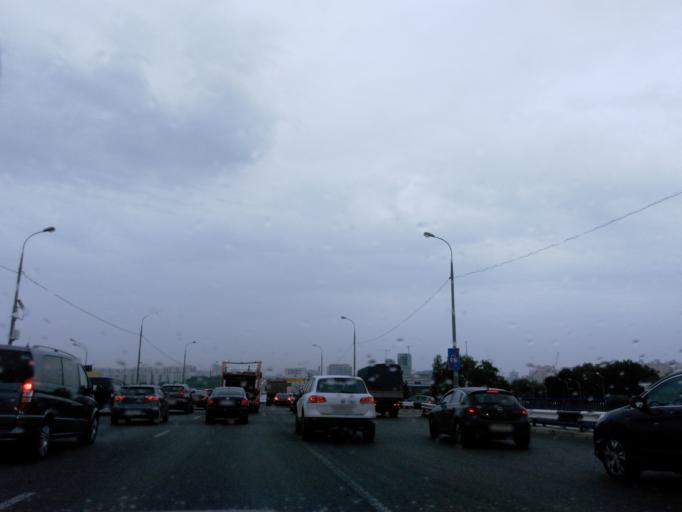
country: RU
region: Moscow
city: Strogino
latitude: 55.8337
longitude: 37.3956
